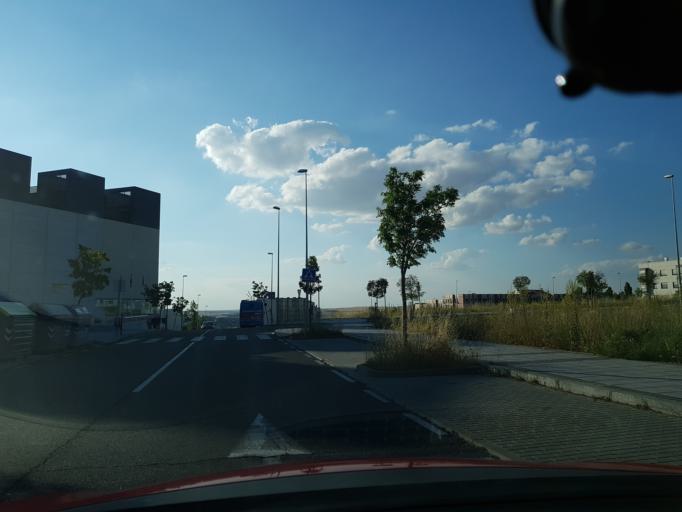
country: ES
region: Castille and Leon
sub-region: Provincia de Segovia
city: Segovia
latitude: 40.9358
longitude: -4.1029
